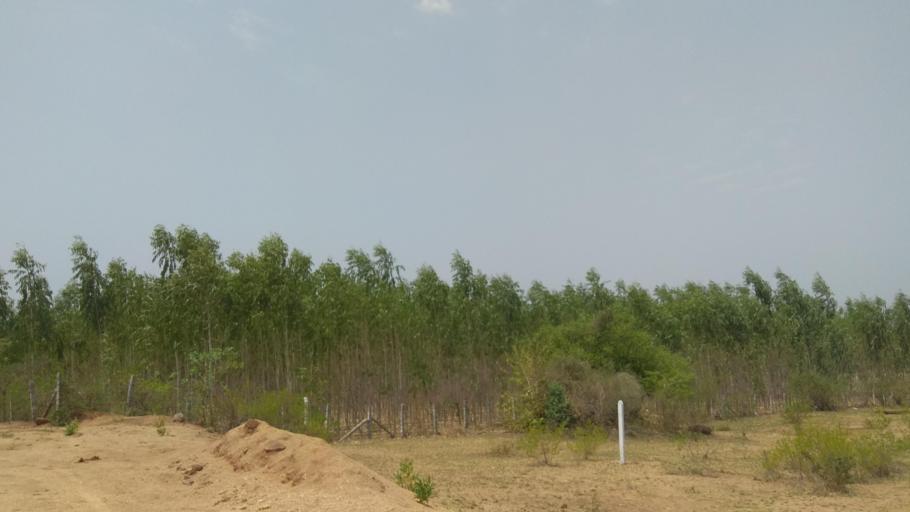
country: IN
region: Telangana
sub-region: Mahbubnagar
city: Farrukhnagar
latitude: 16.8858
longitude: 78.4969
